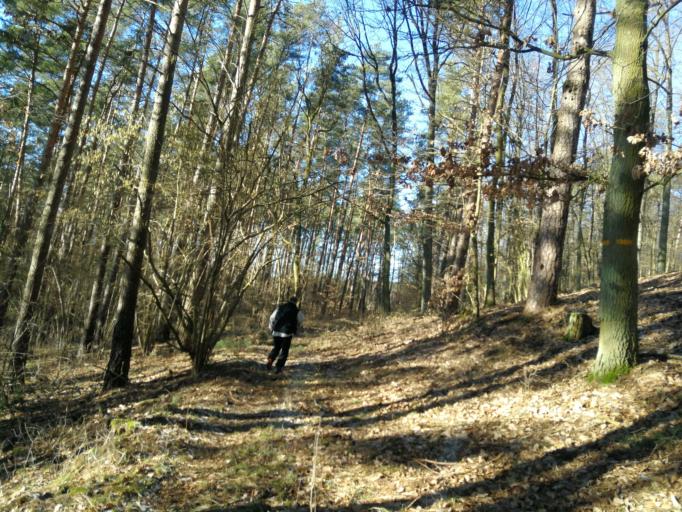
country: PL
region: Kujawsko-Pomorskie
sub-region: Powiat brodnicki
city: Gorzno
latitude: 53.2170
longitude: 19.6673
